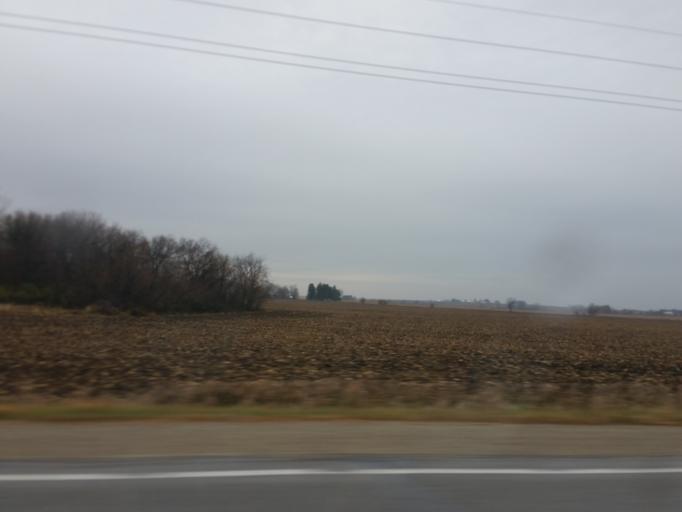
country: US
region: Iowa
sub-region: Black Hawk County
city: Elk Run Heights
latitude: 42.3910
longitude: -92.2502
